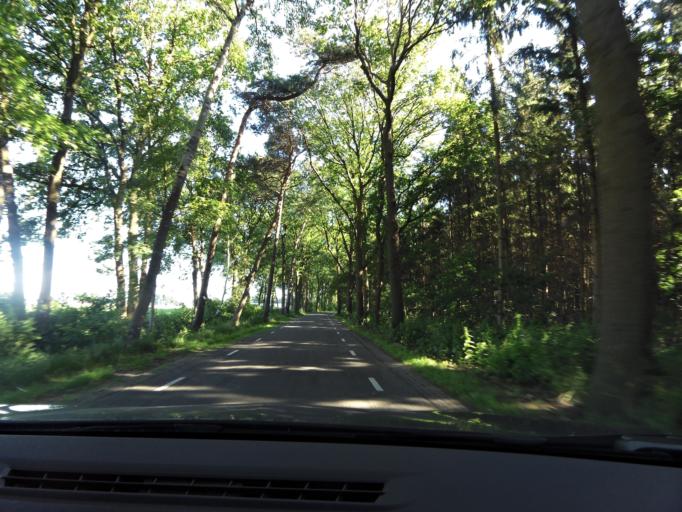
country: NL
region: Overijssel
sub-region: Gemeente Raalte
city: Raalte
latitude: 52.2996
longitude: 6.3059
